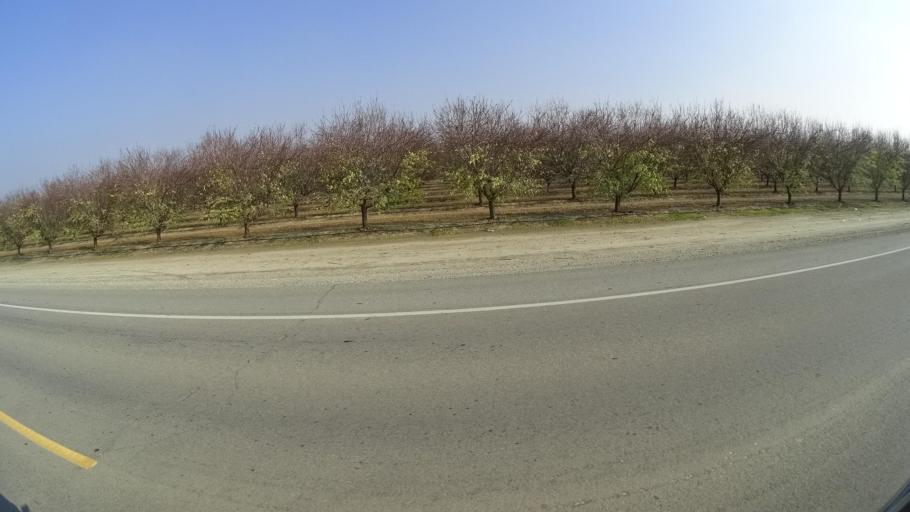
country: US
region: California
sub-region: Kern County
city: Greenfield
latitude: 35.2257
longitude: -119.1099
